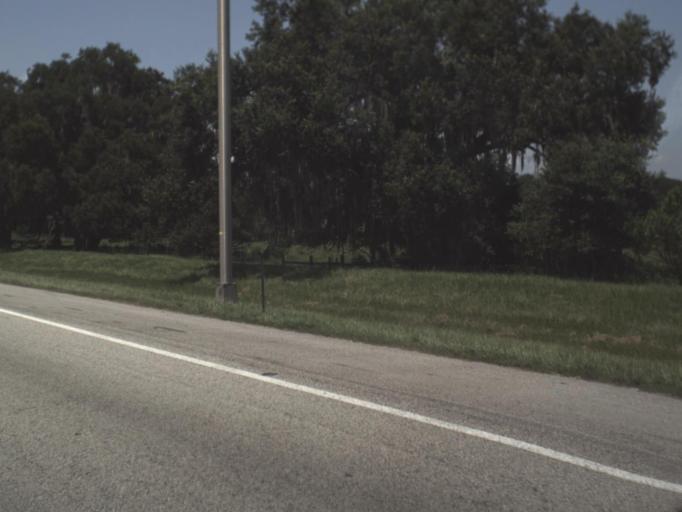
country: US
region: Florida
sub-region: Hillsborough County
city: Seffner
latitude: 28.0191
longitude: -82.2610
